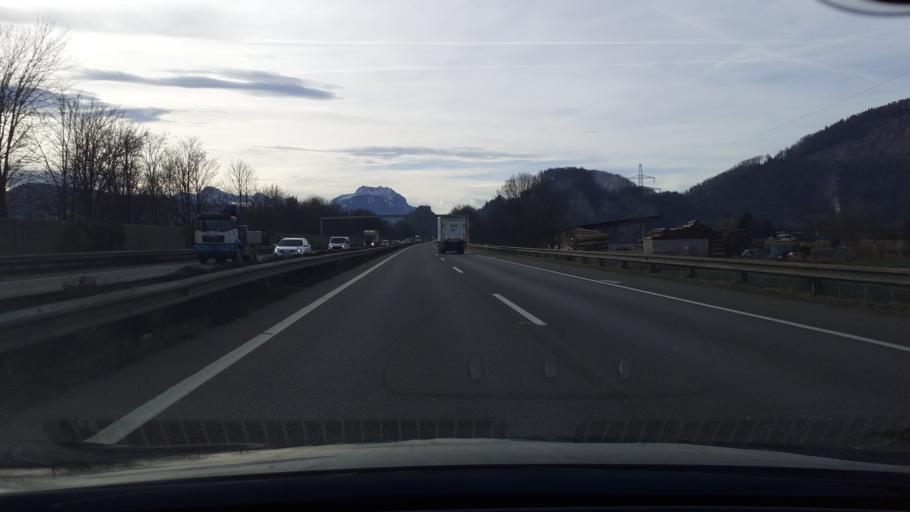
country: AT
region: Vorarlberg
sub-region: Politischer Bezirk Feldkirch
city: Gotzis
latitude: 47.3451
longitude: 9.6351
